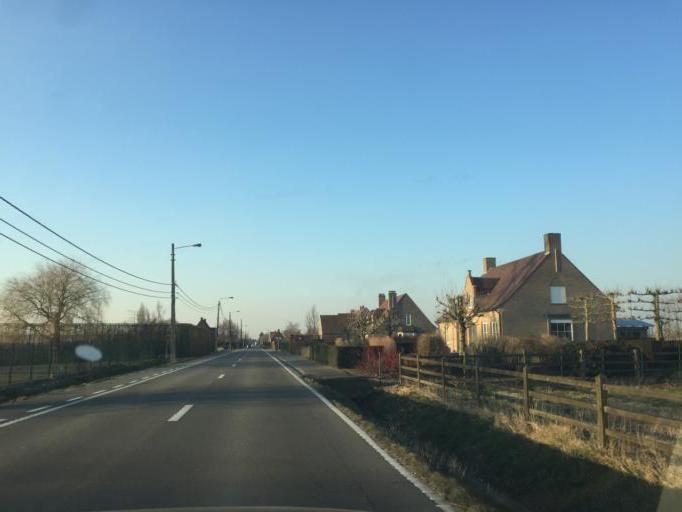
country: BE
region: Flanders
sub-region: Provincie West-Vlaanderen
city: Meulebeke
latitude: 50.9658
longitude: 3.2783
